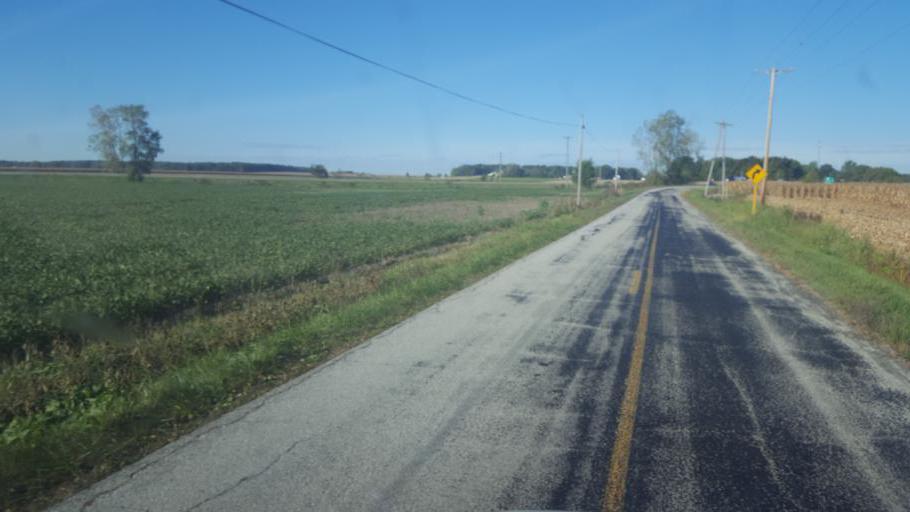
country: US
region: Ohio
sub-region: Marion County
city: Marion
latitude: 40.6882
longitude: -83.1405
